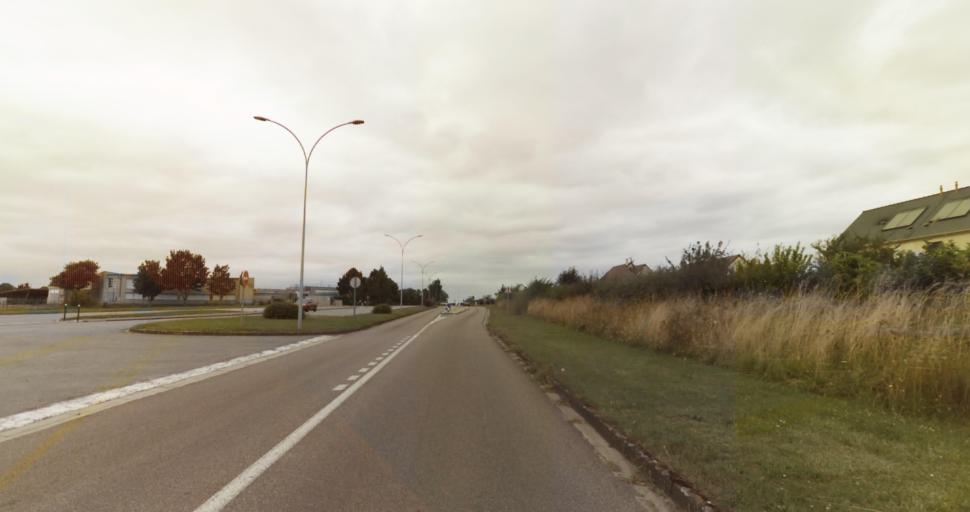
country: FR
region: Haute-Normandie
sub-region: Departement de l'Eure
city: Marcilly-sur-Eure
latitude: 48.9079
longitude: 1.2836
